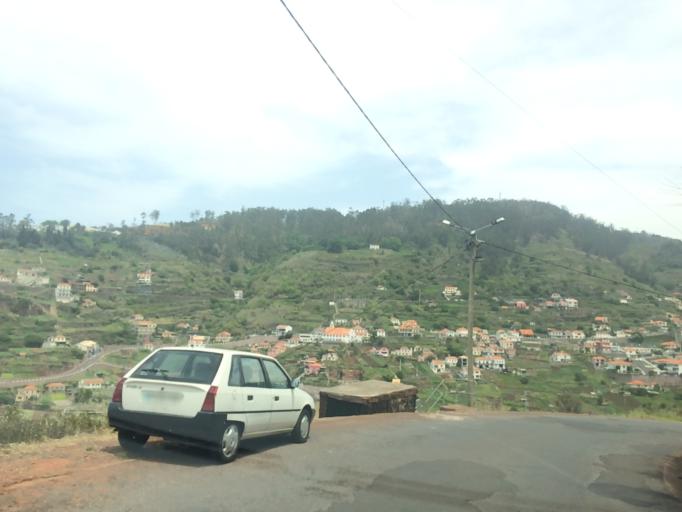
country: PT
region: Madeira
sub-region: Ribeira Brava
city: Campanario
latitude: 32.6577
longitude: -17.0099
